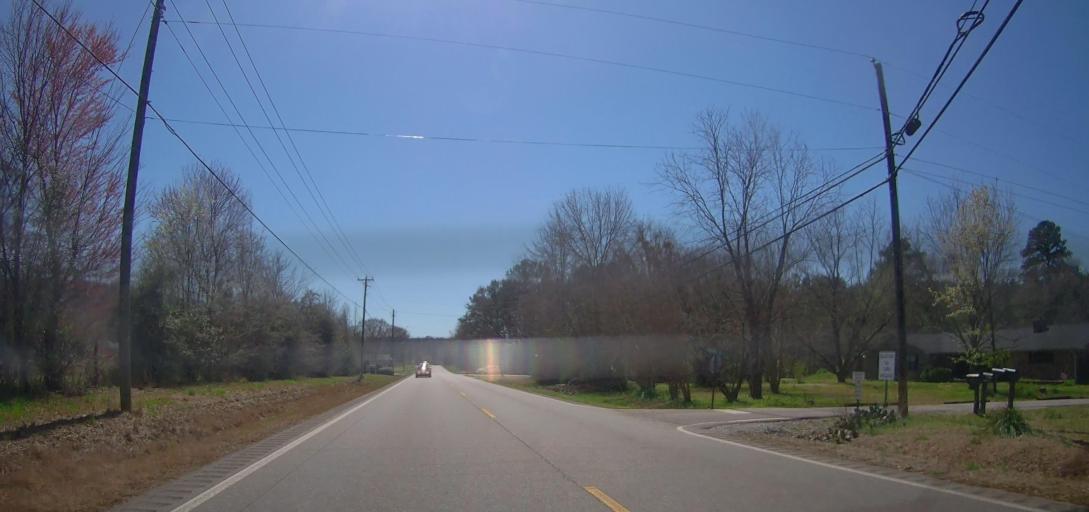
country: US
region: Alabama
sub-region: Etowah County
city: Southside
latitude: 33.8929
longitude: -86.0308
